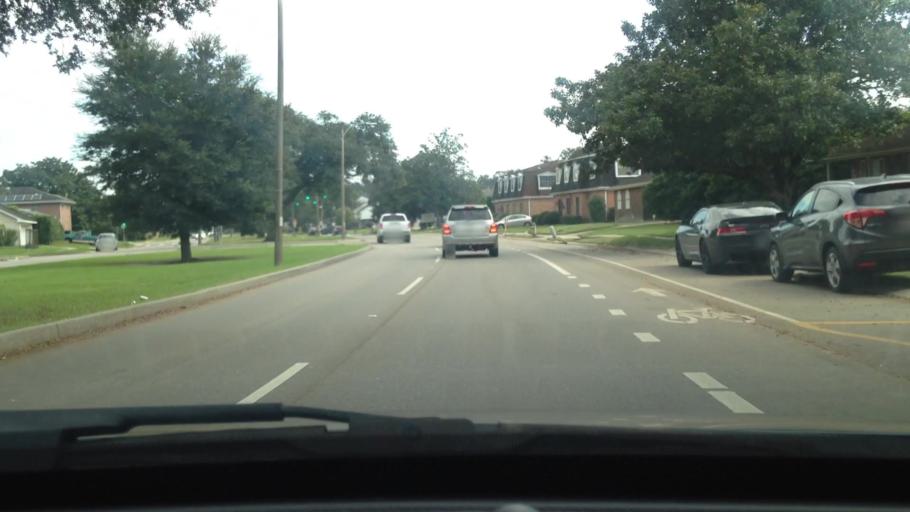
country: US
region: Louisiana
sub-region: Jefferson Parish
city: Terrytown
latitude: 29.9240
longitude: -90.0097
